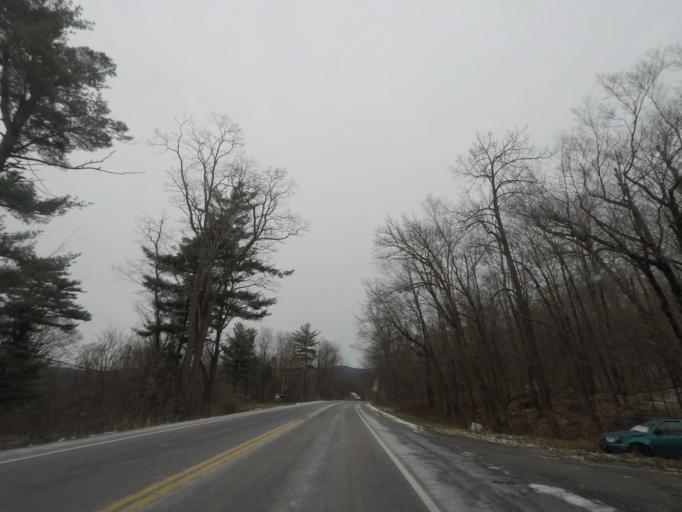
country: US
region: New York
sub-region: Rensselaer County
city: Hoosick Falls
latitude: 42.7600
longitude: -73.3699
